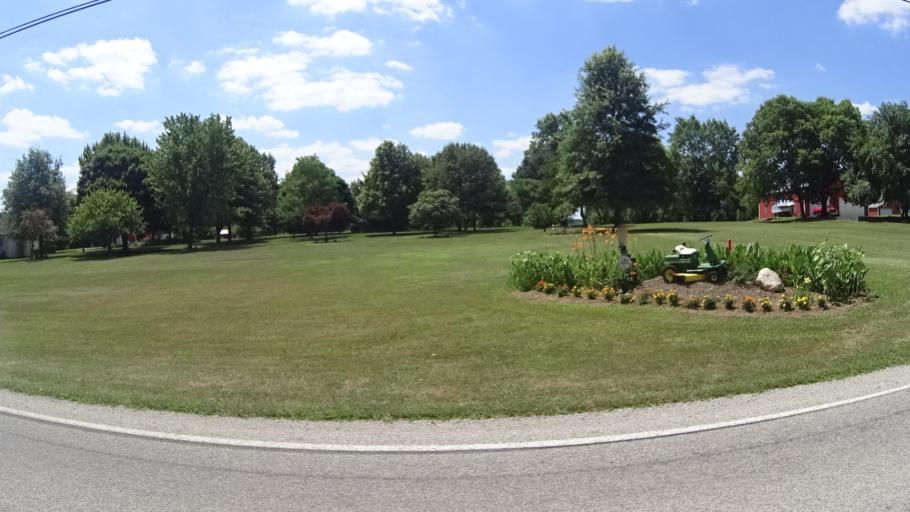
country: US
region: Ohio
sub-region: Erie County
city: Huron
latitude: 41.4009
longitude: -82.6110
